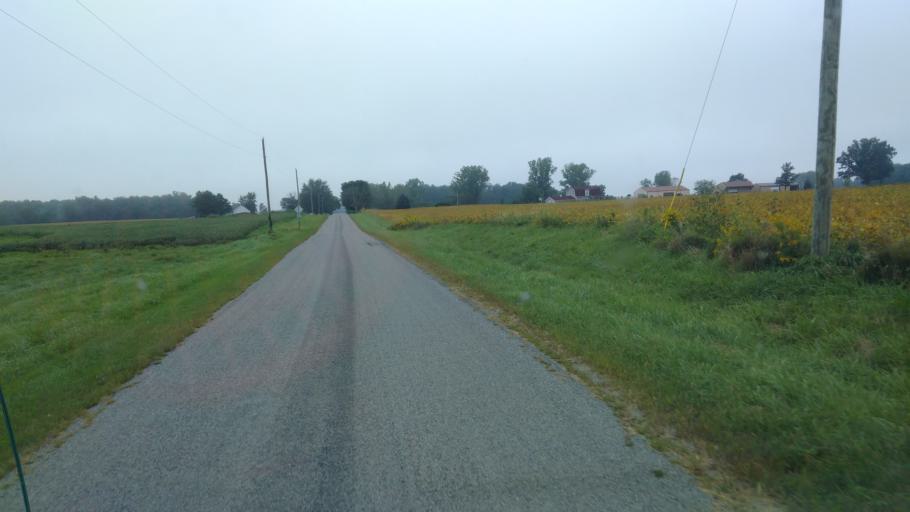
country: US
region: Ohio
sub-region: Union County
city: Richwood
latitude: 40.4857
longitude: -83.4523
